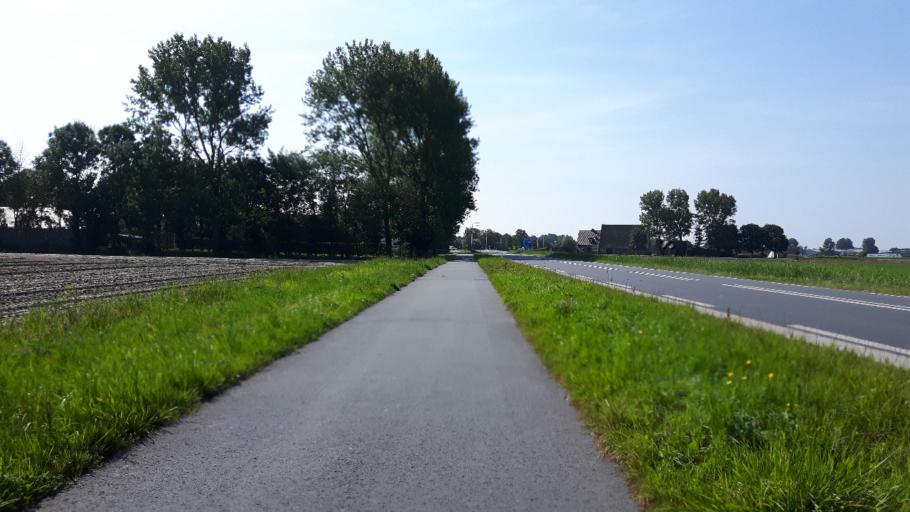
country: NL
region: Friesland
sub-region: Gemeente Ferwerderadiel
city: Hallum
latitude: 53.3125
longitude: 5.7875
